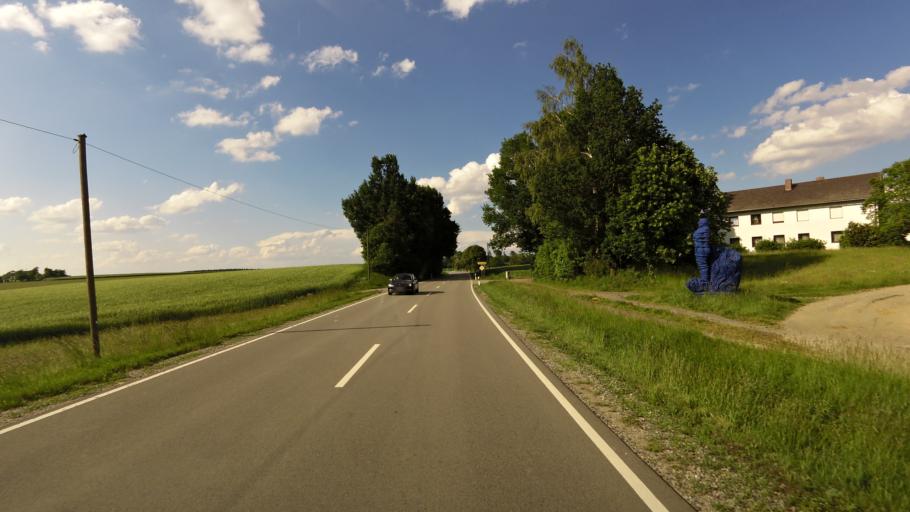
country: DE
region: Bavaria
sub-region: Upper Bavaria
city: Hohenpolding
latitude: 48.4088
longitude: 12.1258
